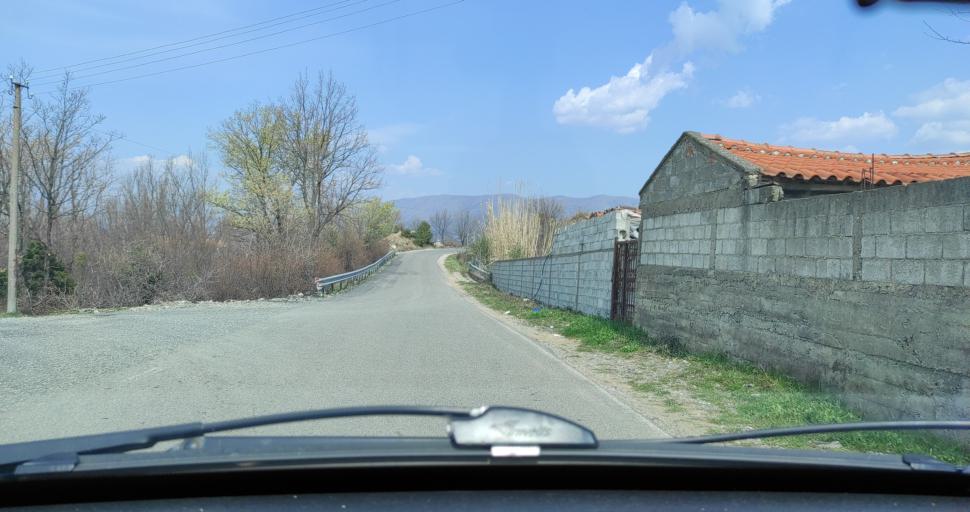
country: AL
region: Lezhe
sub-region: Rrethi i Lezhes
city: Kallmeti i Madh
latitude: 41.8444
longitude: 19.6816
